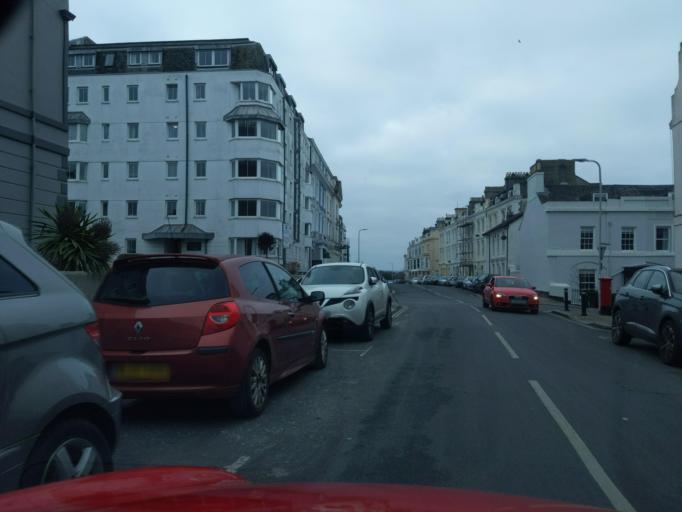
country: GB
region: England
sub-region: Plymouth
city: Plymouth
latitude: 50.3669
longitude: -4.1453
